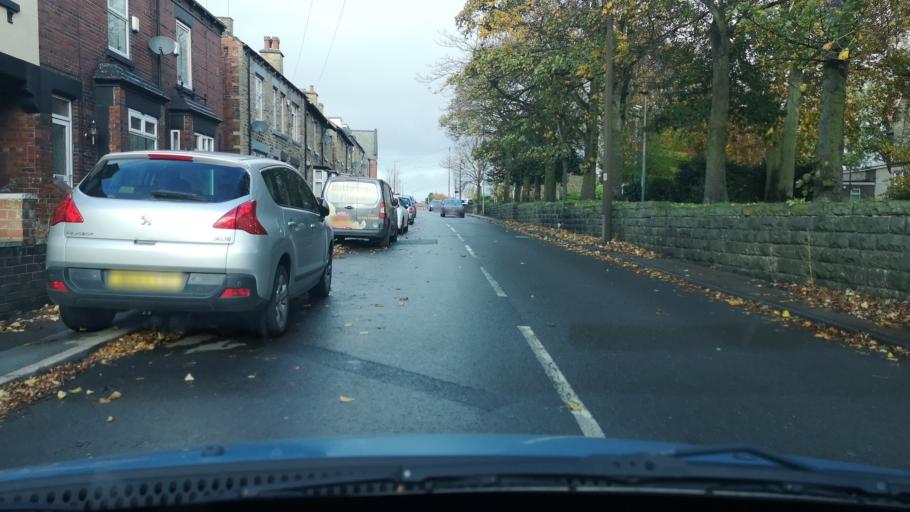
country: GB
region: England
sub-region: Barnsley
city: Royston
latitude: 53.5996
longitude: -1.4562
